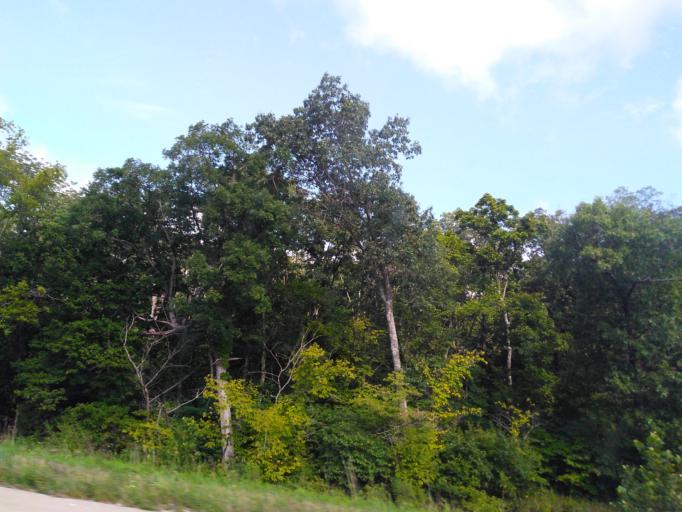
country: US
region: Missouri
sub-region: Jefferson County
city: Hillsboro
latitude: 38.2873
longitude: -90.5502
